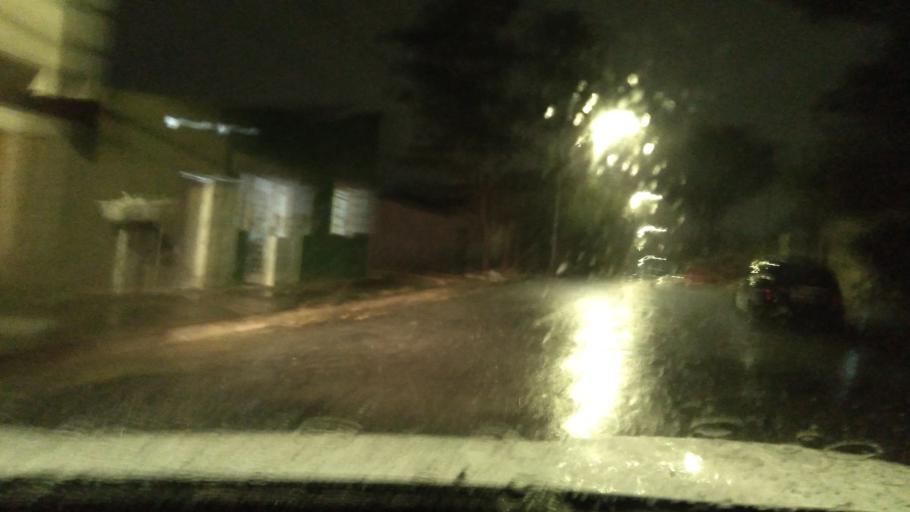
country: BR
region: Minas Gerais
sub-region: Belo Horizonte
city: Belo Horizonte
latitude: -19.8799
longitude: -43.9395
